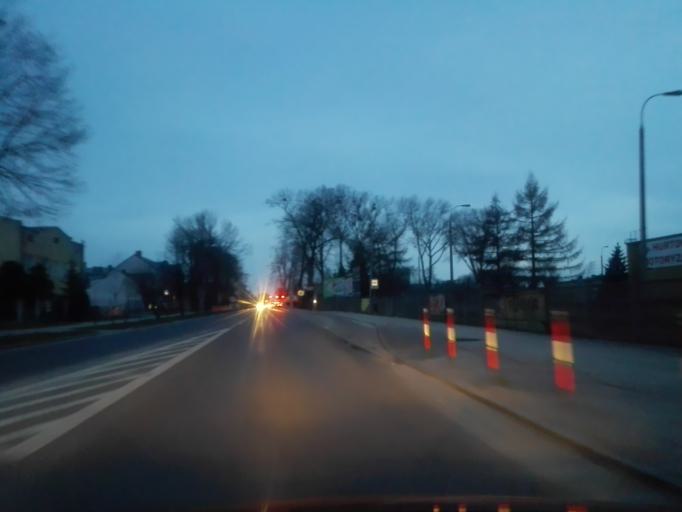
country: PL
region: Podlasie
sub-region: Lomza
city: Lomza
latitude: 53.1682
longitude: 22.0636
